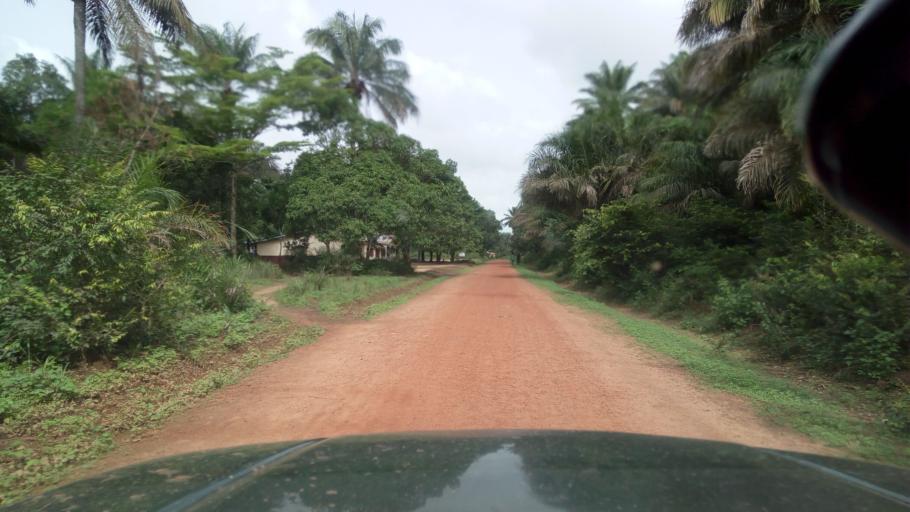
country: SL
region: Northern Province
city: Mange
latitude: 8.8364
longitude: -12.9367
